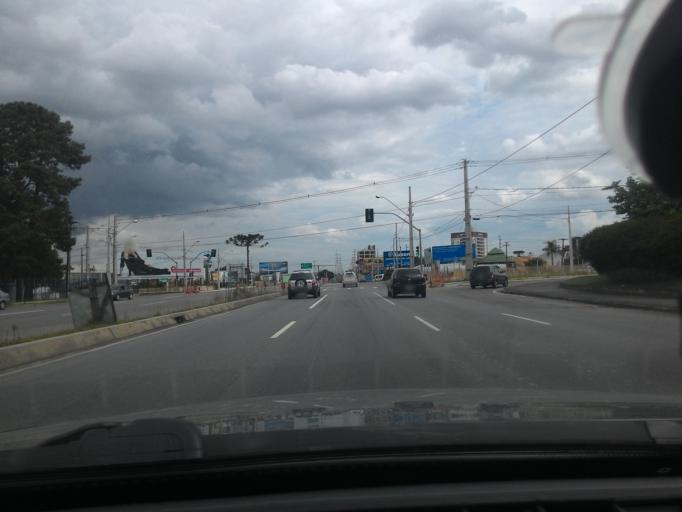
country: BR
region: Parana
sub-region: Sao Jose Dos Pinhais
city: Sao Jose dos Pinhais
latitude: -25.5317
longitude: -49.1954
